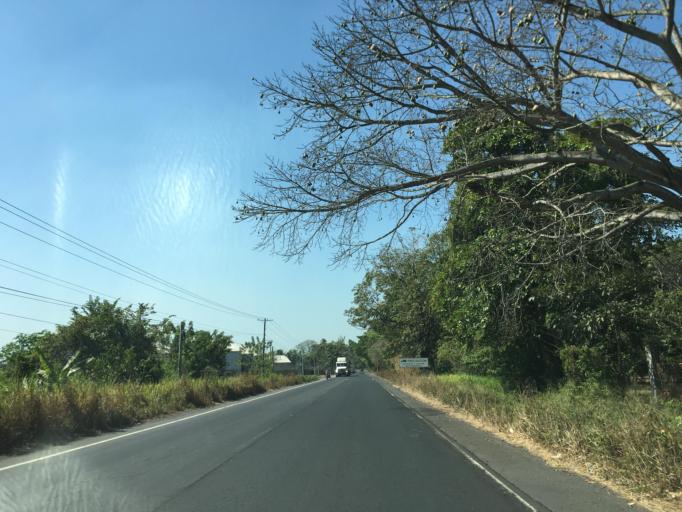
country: GT
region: Escuintla
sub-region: Municipio de Masagua
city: Masagua
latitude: 14.1661
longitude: -90.8785
